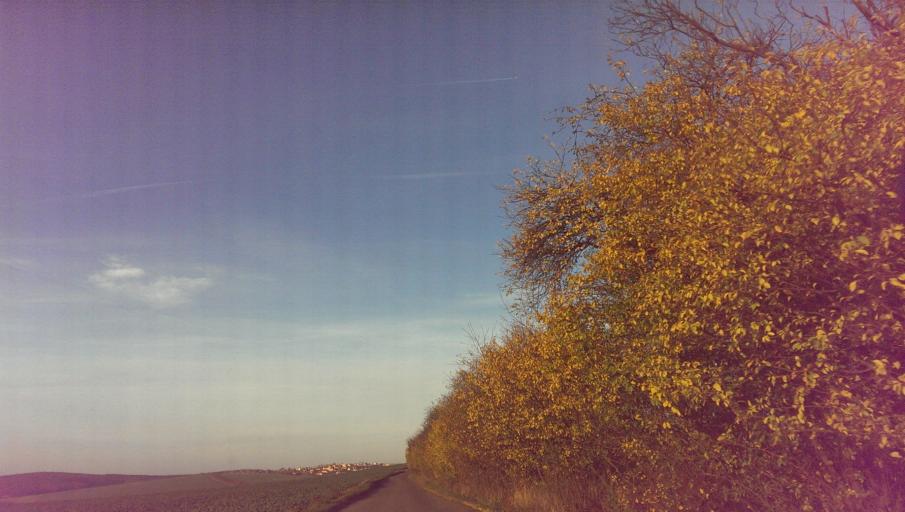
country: CZ
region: Zlin
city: Brezolupy
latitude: 49.1483
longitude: 17.5959
